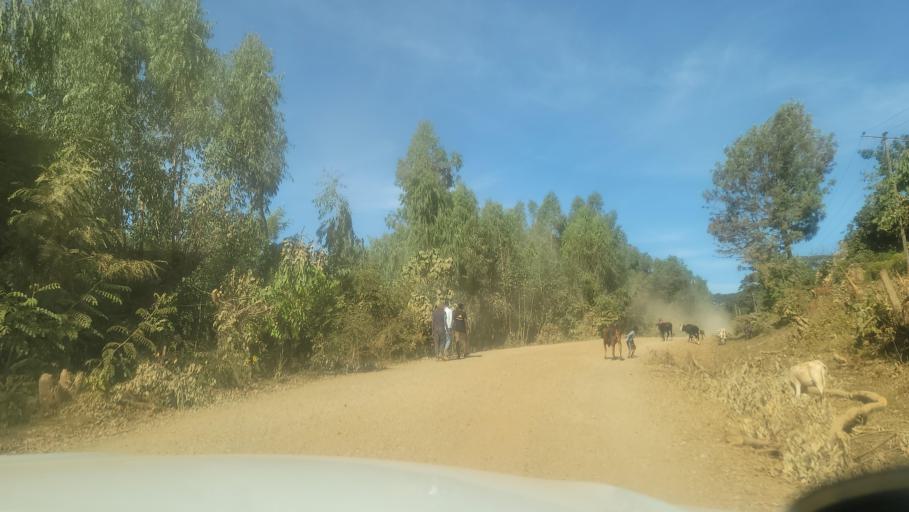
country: ET
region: Oromiya
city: Agaro
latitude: 7.8139
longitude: 36.5112
